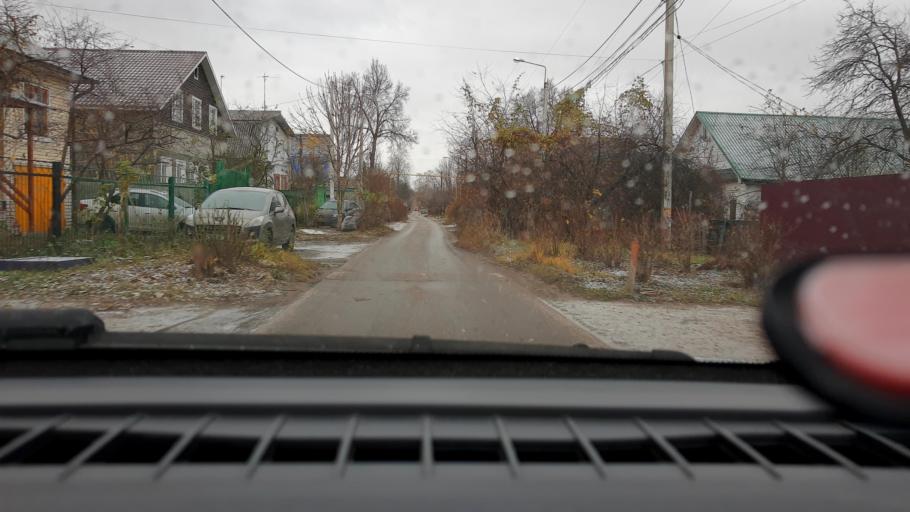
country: RU
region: Nizjnij Novgorod
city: Burevestnik
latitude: 56.2014
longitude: 43.7883
